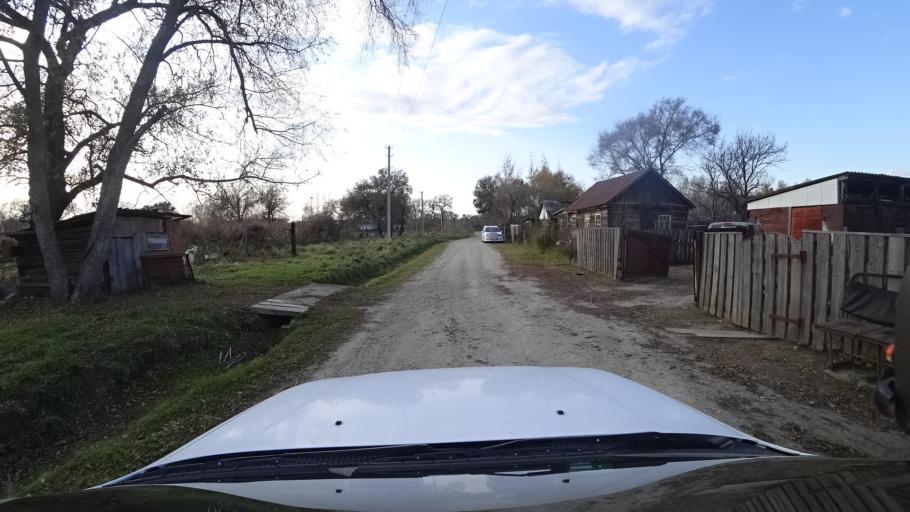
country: RU
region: Primorskiy
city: Lazo
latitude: 45.8215
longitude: 133.6165
